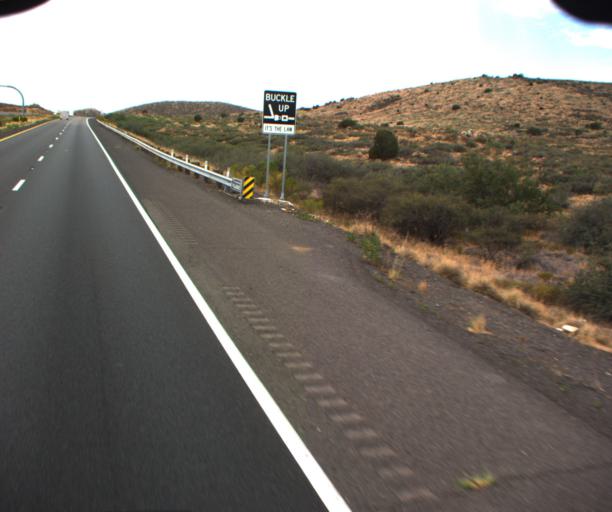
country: US
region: Arizona
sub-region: Yavapai County
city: Cordes Lakes
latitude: 34.3152
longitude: -112.1245
